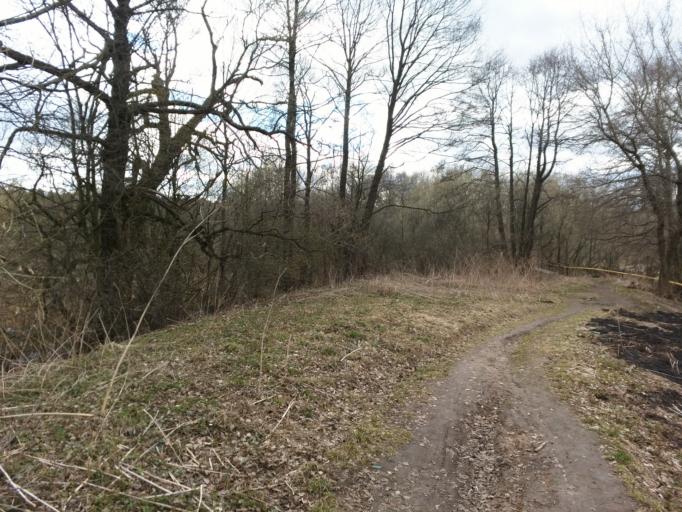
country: RU
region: Moskovskaya
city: Saltykovka
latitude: 55.7749
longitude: 37.9485
